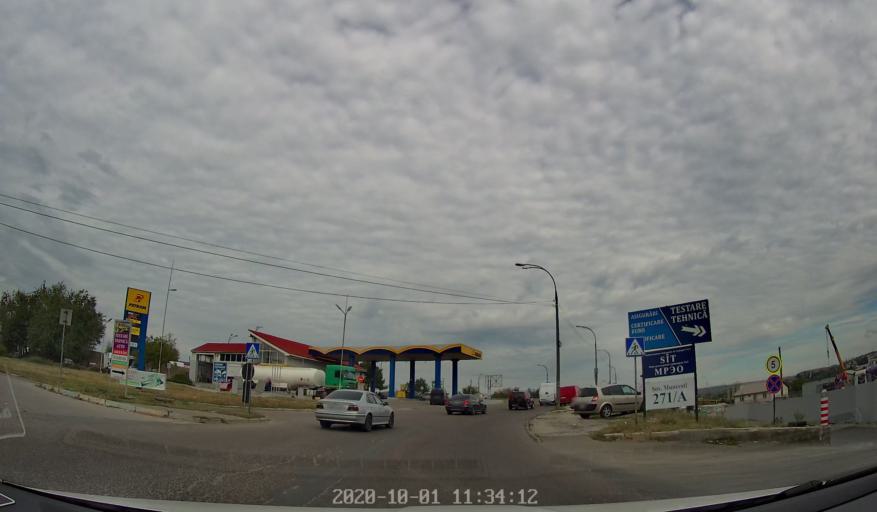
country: MD
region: Chisinau
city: Chisinau
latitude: 46.9801
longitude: 28.9022
